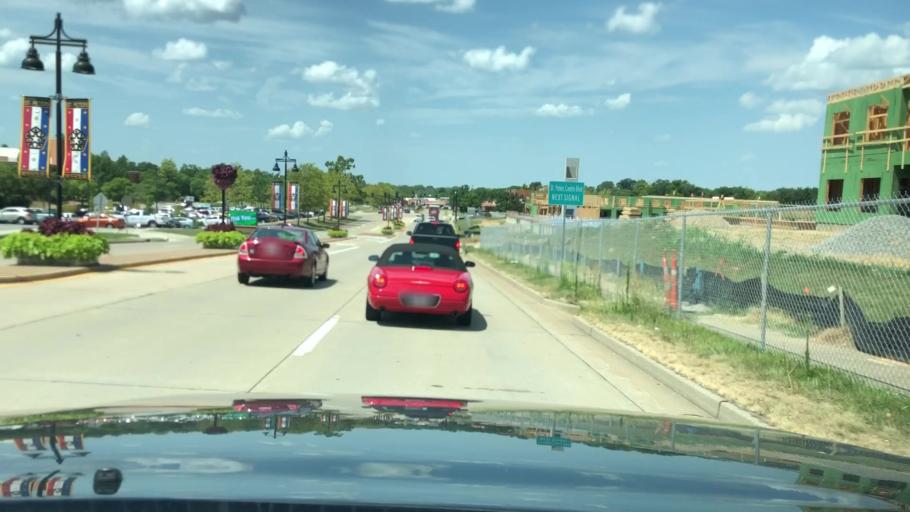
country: US
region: Missouri
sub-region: Saint Charles County
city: Saint Peters
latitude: 38.7927
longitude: -90.5929
